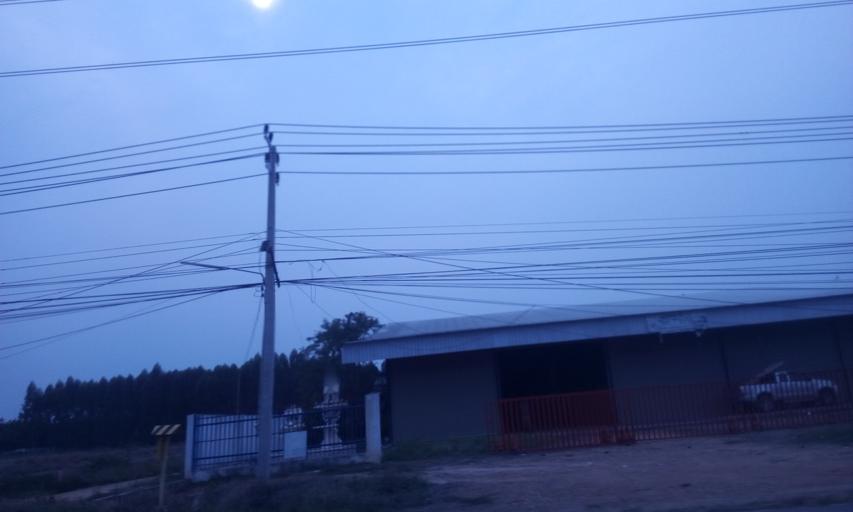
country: TH
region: Chon Buri
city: Ko Chan
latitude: 13.4546
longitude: 101.2837
